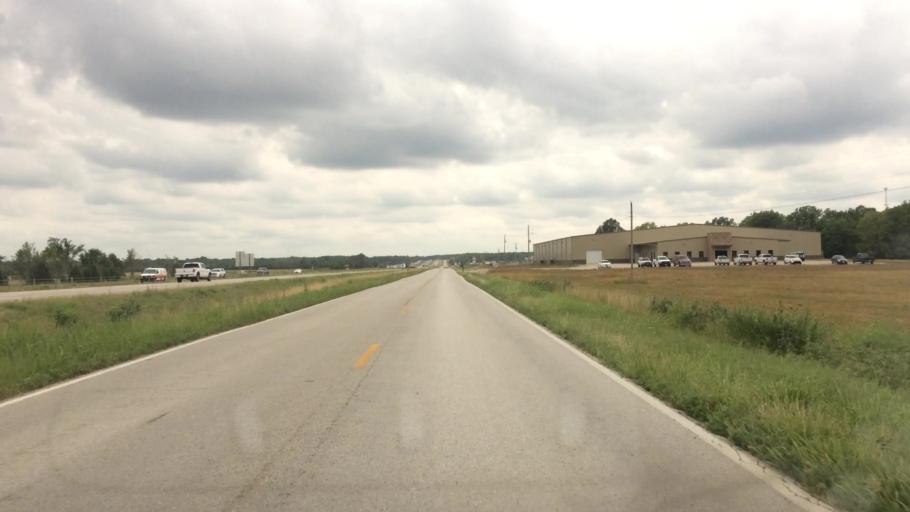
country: US
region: Missouri
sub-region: Greene County
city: Strafford
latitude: 37.2974
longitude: -93.0176
